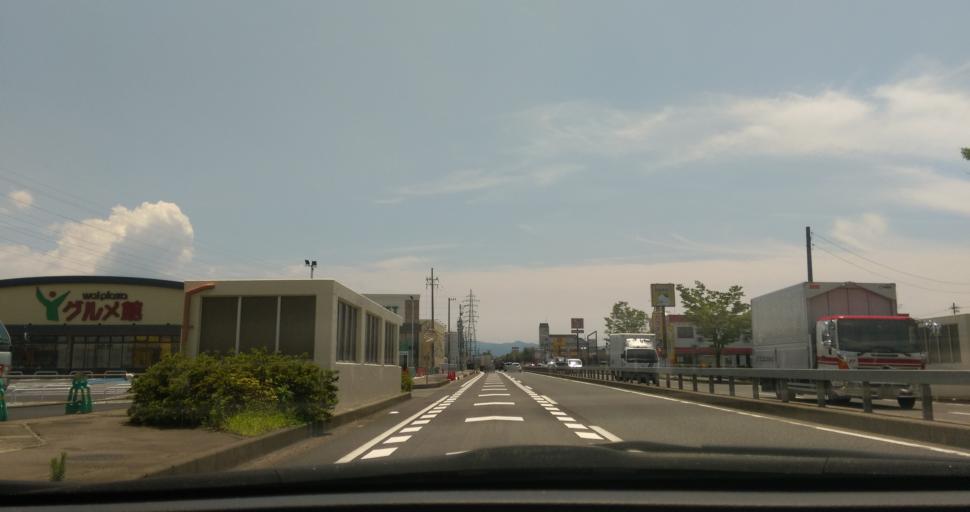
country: JP
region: Fukui
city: Sabae
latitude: 35.9418
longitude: 136.1931
